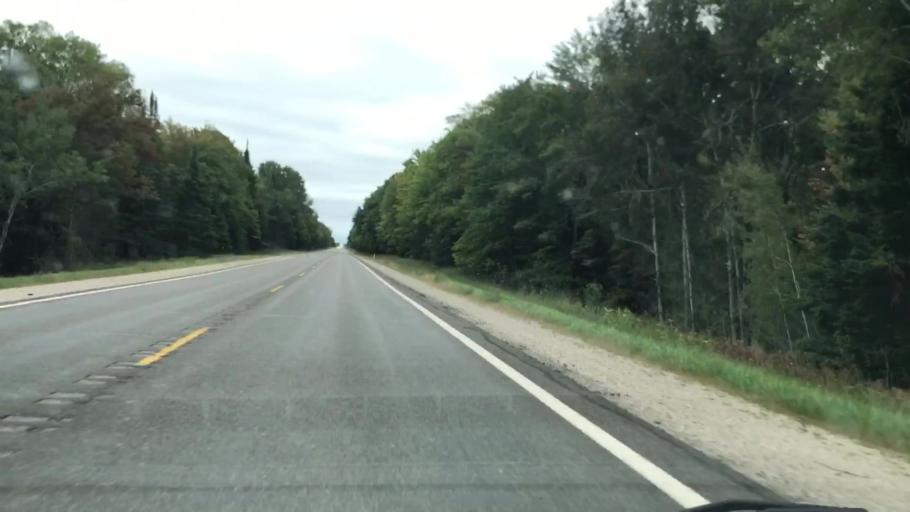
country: US
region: Michigan
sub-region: Luce County
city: Newberry
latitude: 46.2297
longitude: -85.5721
